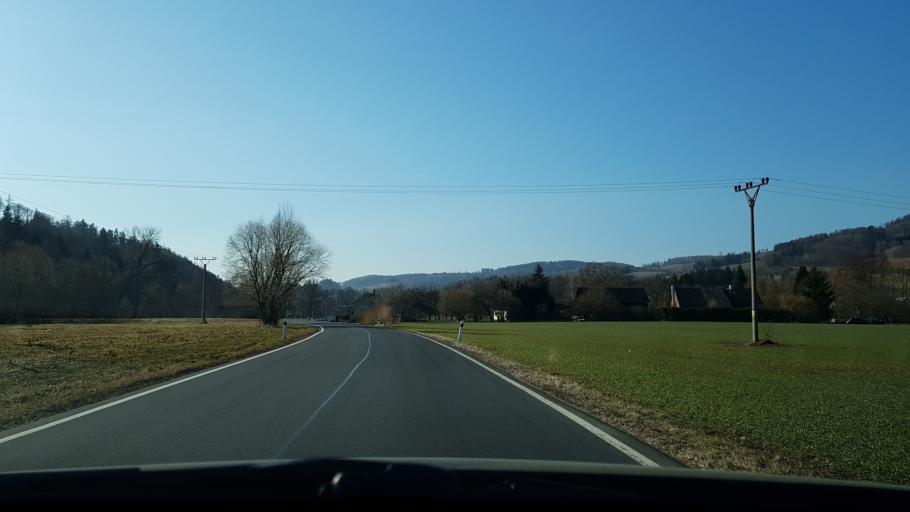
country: CZ
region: Olomoucky
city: Dolni Bohdikov
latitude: 50.0337
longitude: 16.9056
